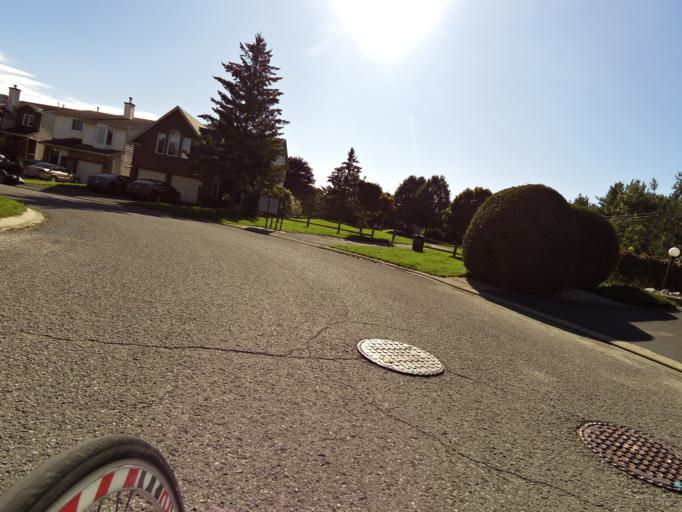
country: CA
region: Ontario
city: Bells Corners
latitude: 45.3136
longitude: -75.8371
